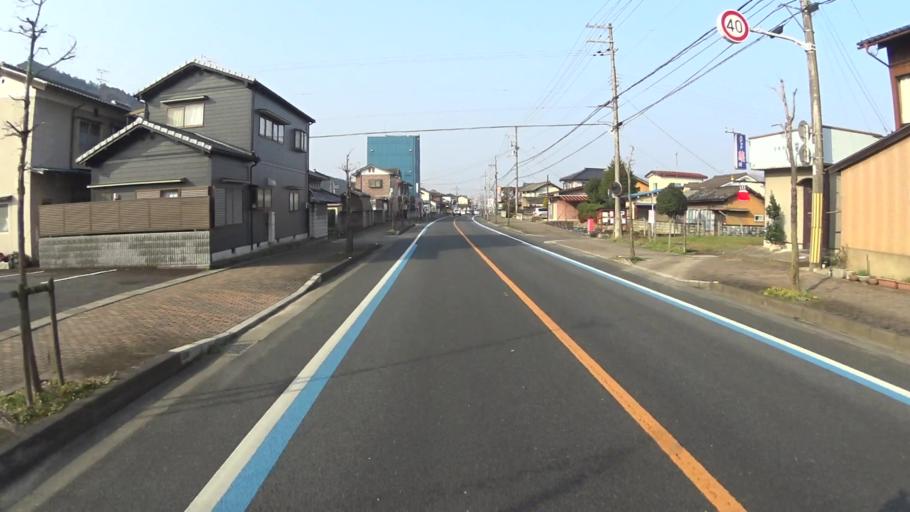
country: JP
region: Kyoto
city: Ayabe
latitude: 35.3033
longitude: 135.2298
